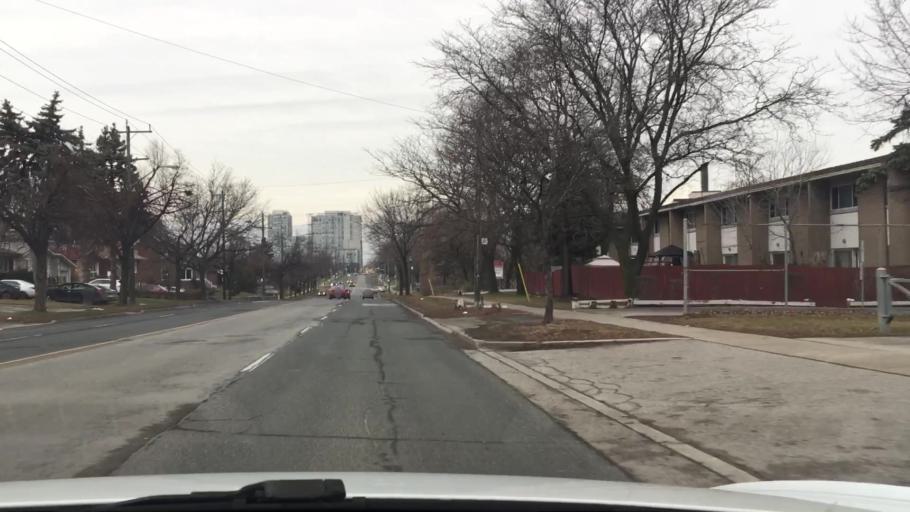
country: CA
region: Ontario
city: Scarborough
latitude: 43.7440
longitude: -79.2620
